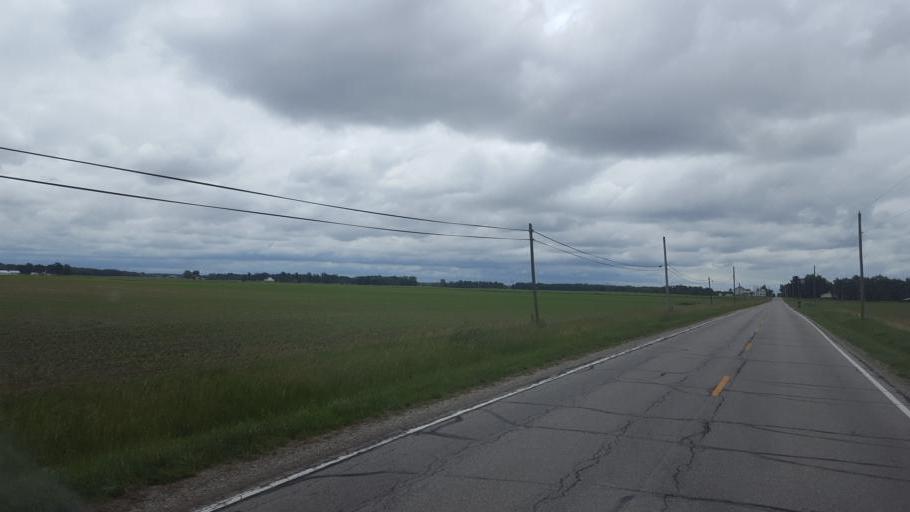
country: US
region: Ohio
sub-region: Crawford County
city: Bucyrus
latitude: 40.7665
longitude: -82.9540
